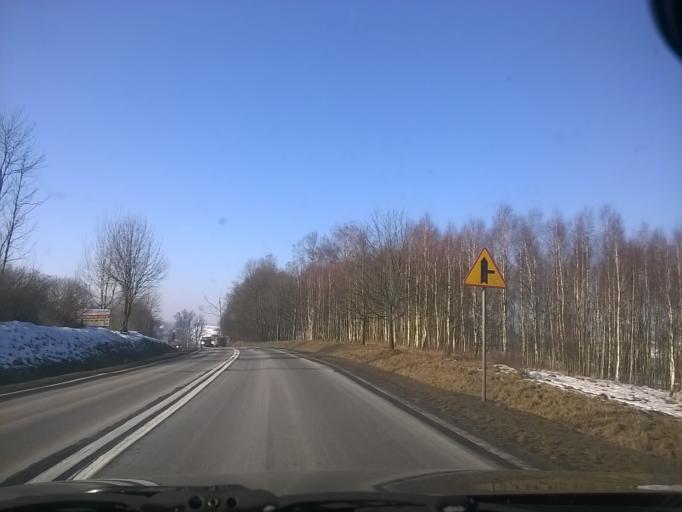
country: PL
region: Warmian-Masurian Voivodeship
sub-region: Powiat mragowski
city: Mragowo
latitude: 53.8396
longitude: 21.1825
